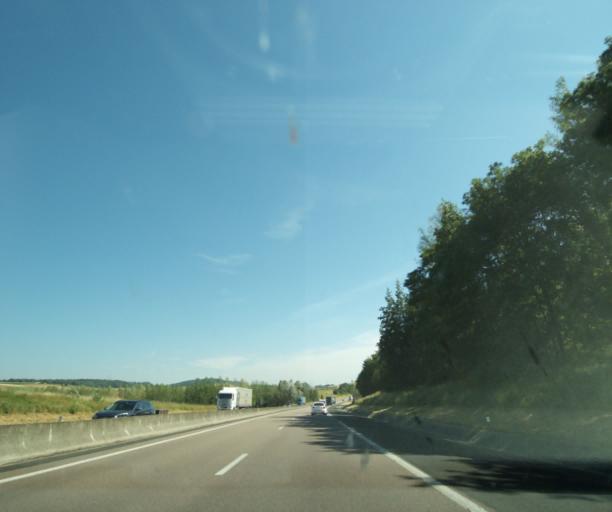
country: FR
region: Lorraine
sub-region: Departement des Vosges
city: Chatenois
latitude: 48.3472
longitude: 5.8555
